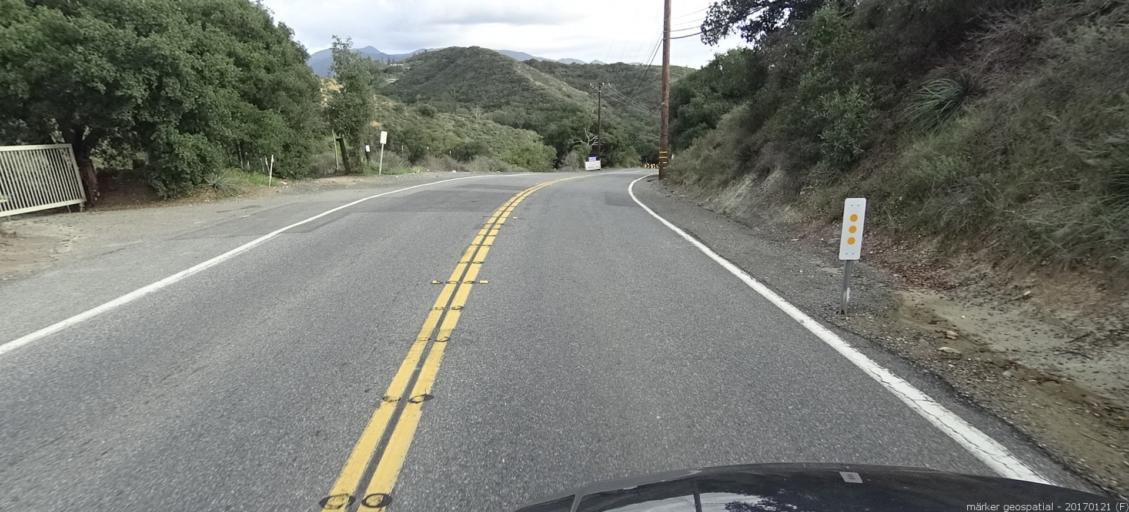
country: US
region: California
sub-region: Orange County
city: Portola Hills
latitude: 33.6852
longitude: -117.6056
